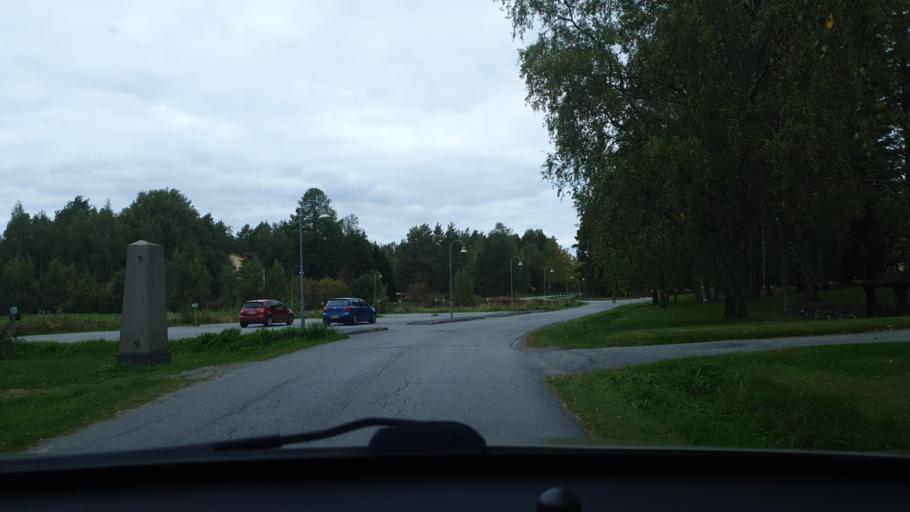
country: FI
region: Ostrobothnia
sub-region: Vaasa
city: Teeriniemi
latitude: 63.0873
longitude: 21.6746
